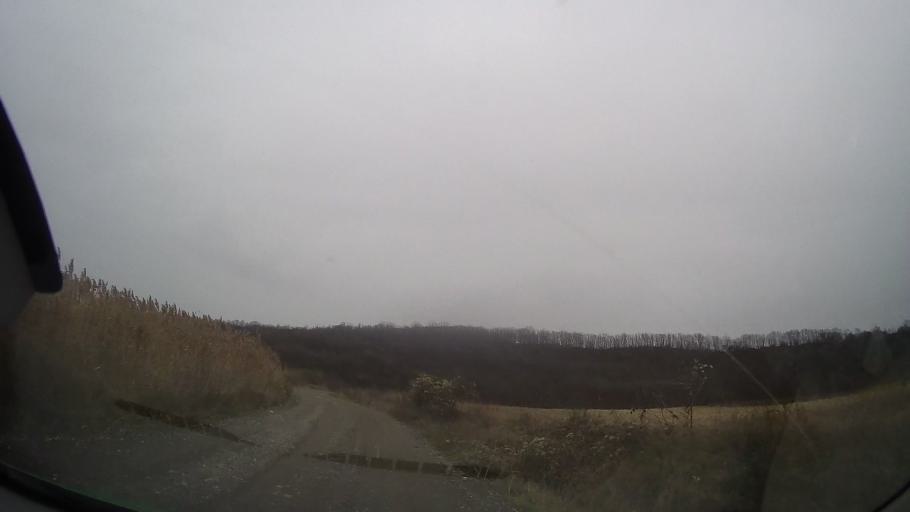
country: RO
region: Mures
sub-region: Comuna Ceausu de Campie
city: Ceausu de Campie
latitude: 46.6507
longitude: 24.4974
